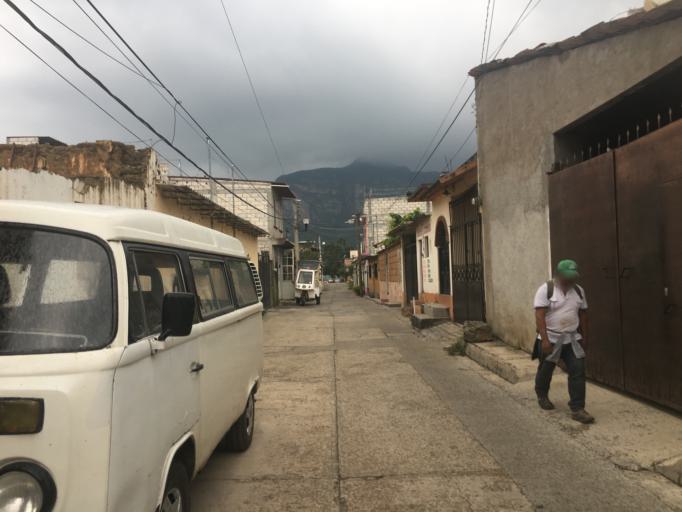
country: MX
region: Morelos
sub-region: Tlayacapan
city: Tlayacapan
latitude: 18.9597
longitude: -98.9824
